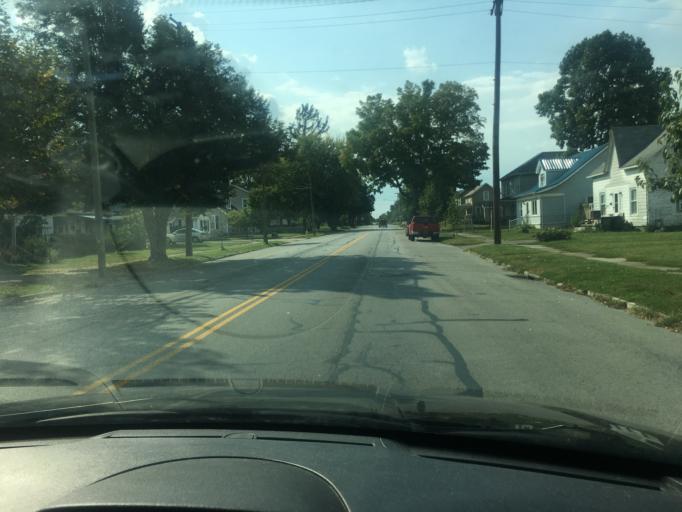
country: US
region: Ohio
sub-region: Champaign County
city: Urbana
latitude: 40.1091
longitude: -83.7675
